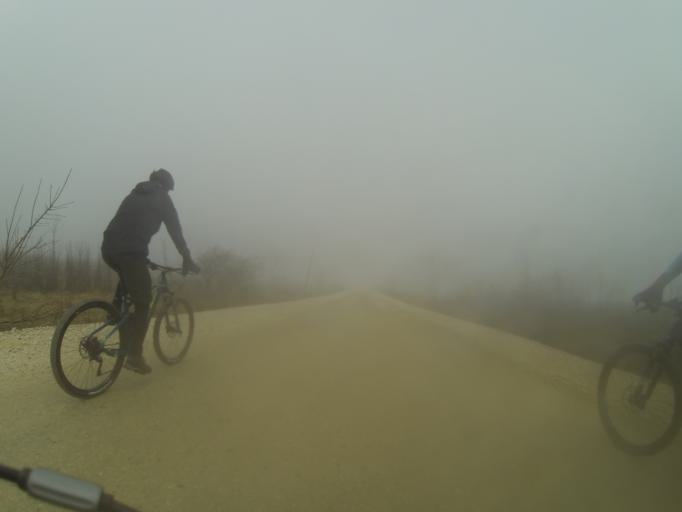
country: RO
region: Mehedinti
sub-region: Comuna Baclesu
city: Baclesu
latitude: 44.4614
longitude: 23.1148
